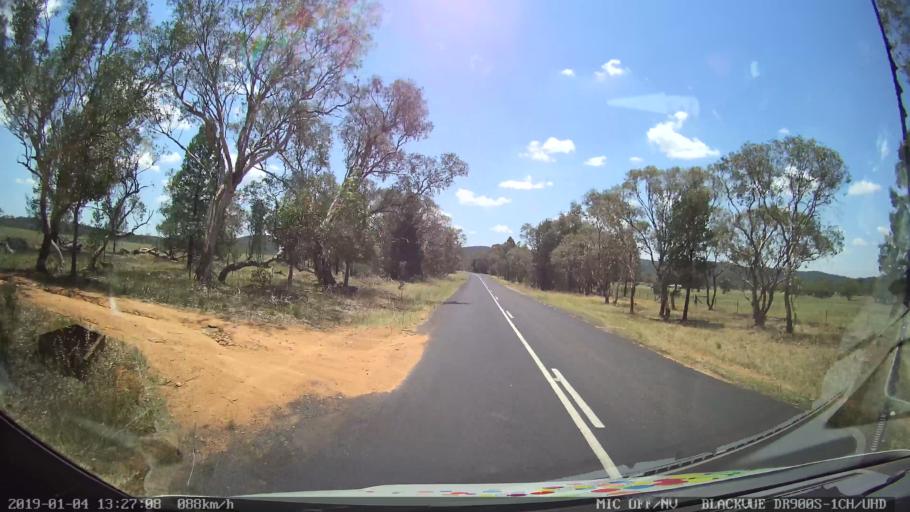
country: AU
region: New South Wales
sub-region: Parkes
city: Peak Hill
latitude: -32.6727
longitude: 148.5610
